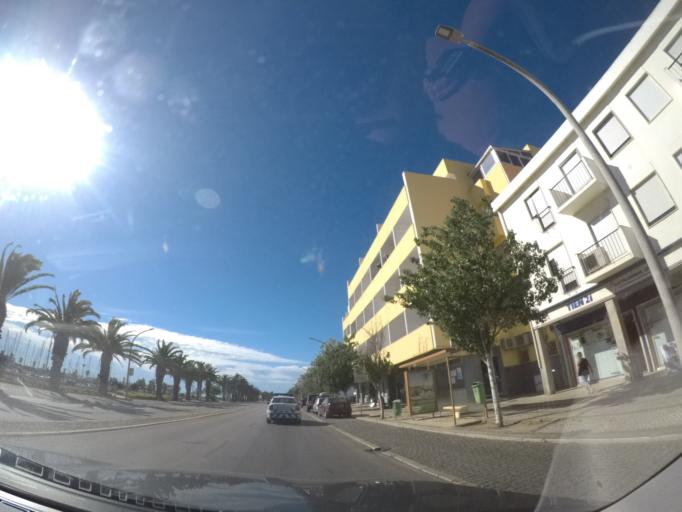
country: PT
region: Faro
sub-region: Lagos
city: Lagos
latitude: 37.1095
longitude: -8.6766
